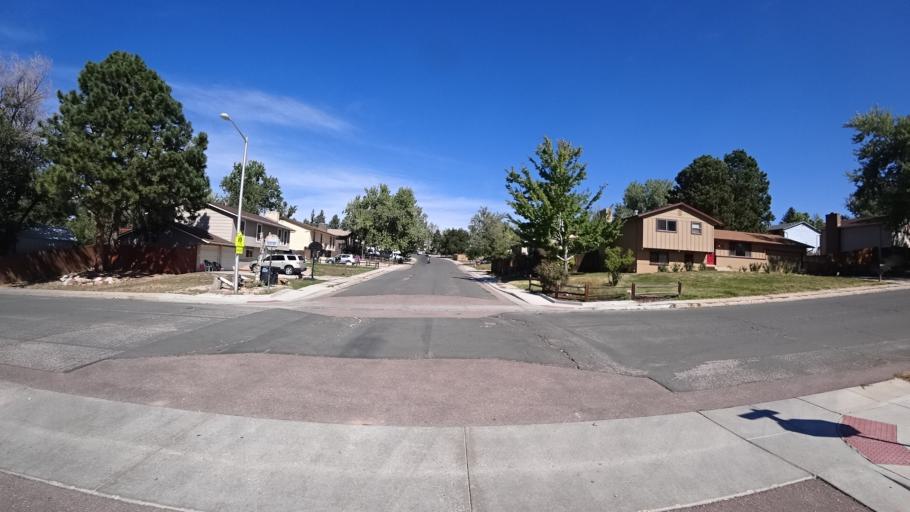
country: US
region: Colorado
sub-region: El Paso County
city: Cimarron Hills
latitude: 38.9080
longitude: -104.7691
